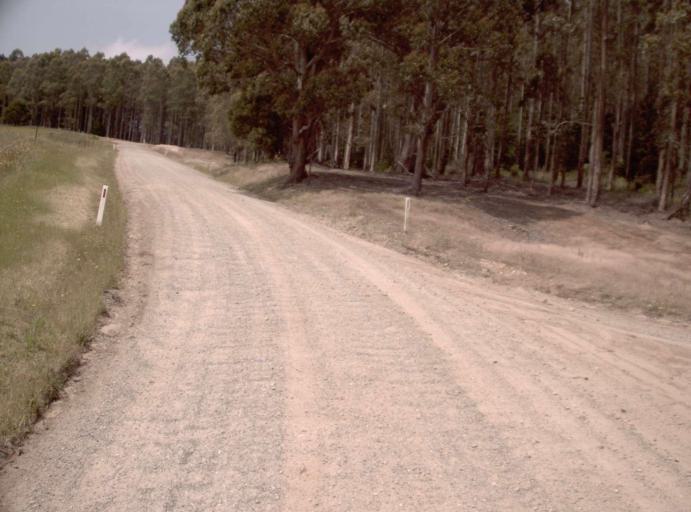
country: AU
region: Victoria
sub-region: Latrobe
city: Traralgon
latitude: -38.3785
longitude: 146.6735
